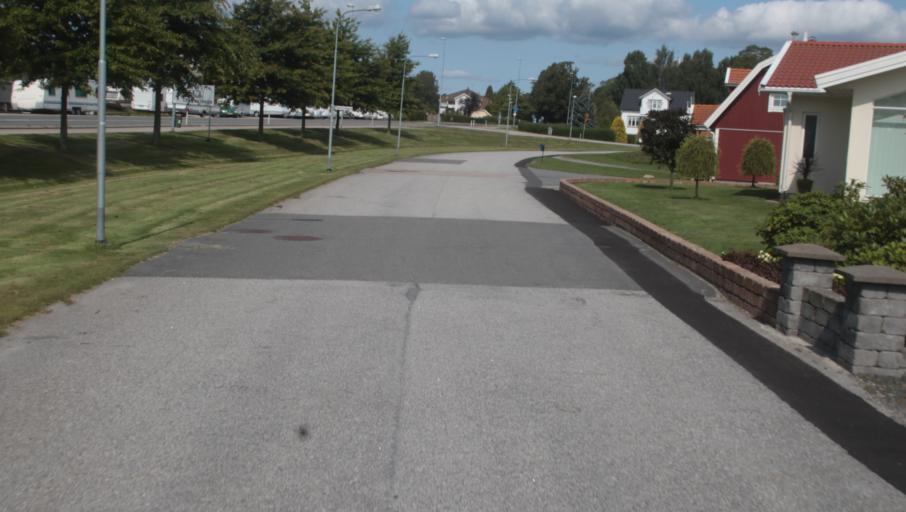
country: SE
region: Blekinge
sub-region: Karlshamns Kommun
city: Karlshamn
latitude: 56.2008
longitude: 14.8362
